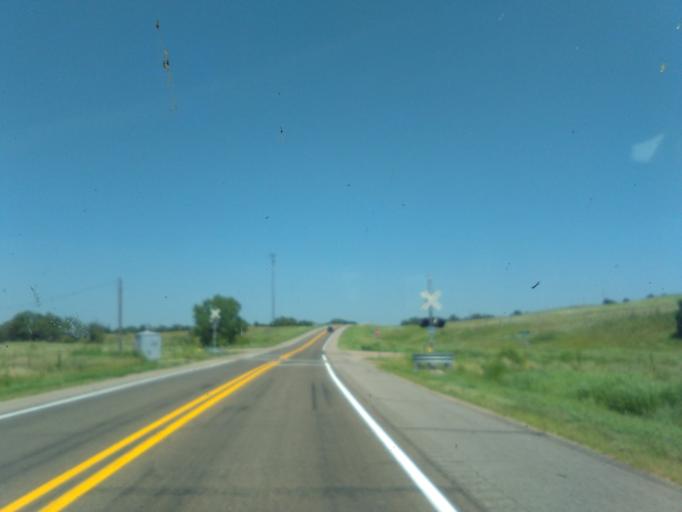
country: US
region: Nebraska
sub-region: Hayes County
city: Hayes Center
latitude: 40.7469
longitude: -100.7239
